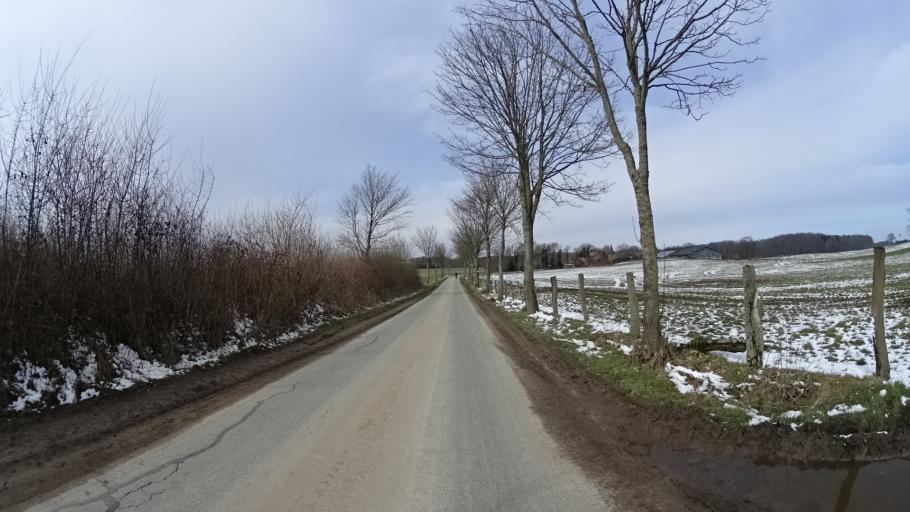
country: DE
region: Schleswig-Holstein
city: Rendswuhren
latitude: 54.0935
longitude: 10.1947
